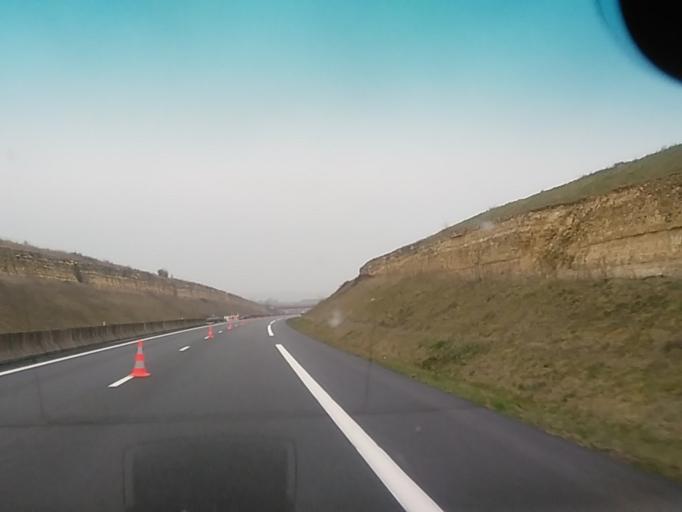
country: FR
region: Lower Normandy
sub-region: Departement de l'Orne
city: Gace
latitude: 48.6988
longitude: 0.2409
